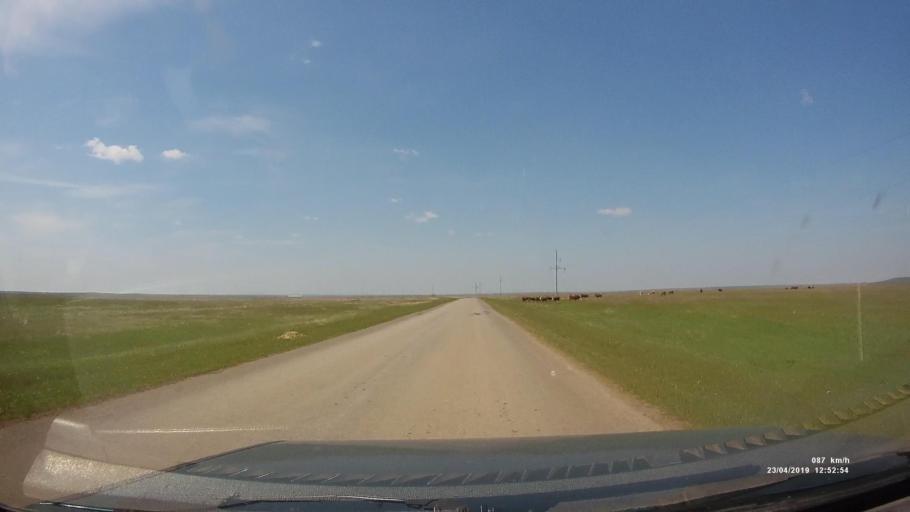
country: RU
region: Kalmykiya
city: Yashalta
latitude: 46.5690
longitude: 42.6036
